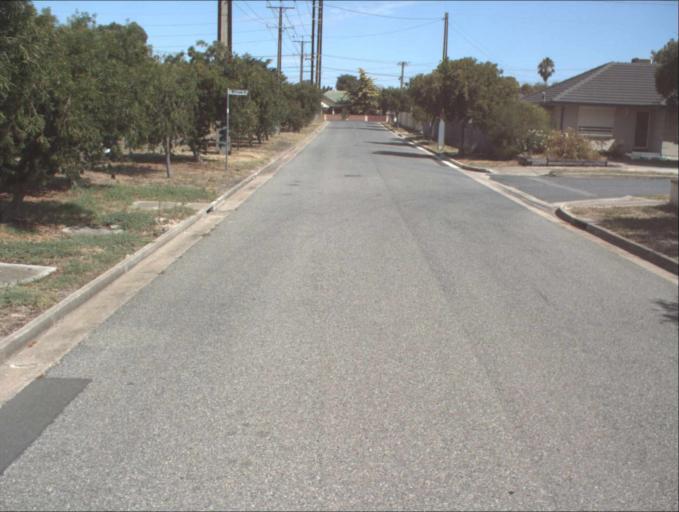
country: AU
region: South Australia
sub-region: Port Adelaide Enfield
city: Birkenhead
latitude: -34.7950
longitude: 138.5038
